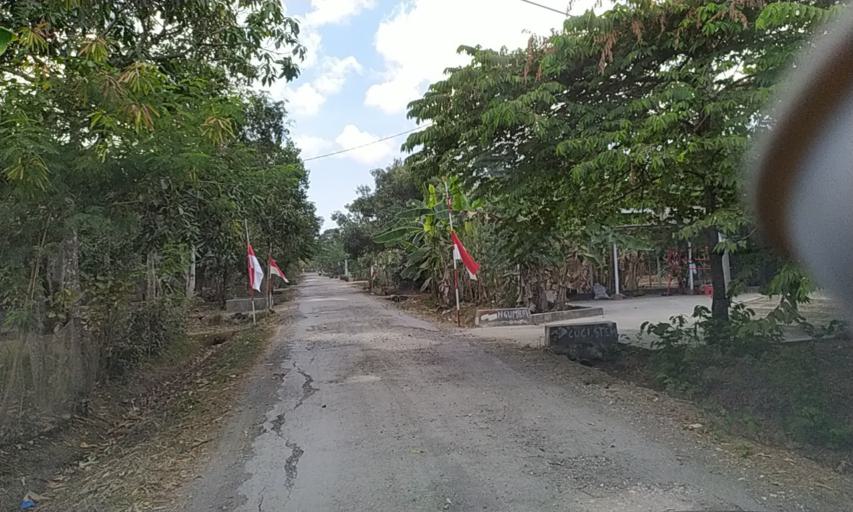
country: ID
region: Central Java
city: Patimuan
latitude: -7.5971
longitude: 108.7430
